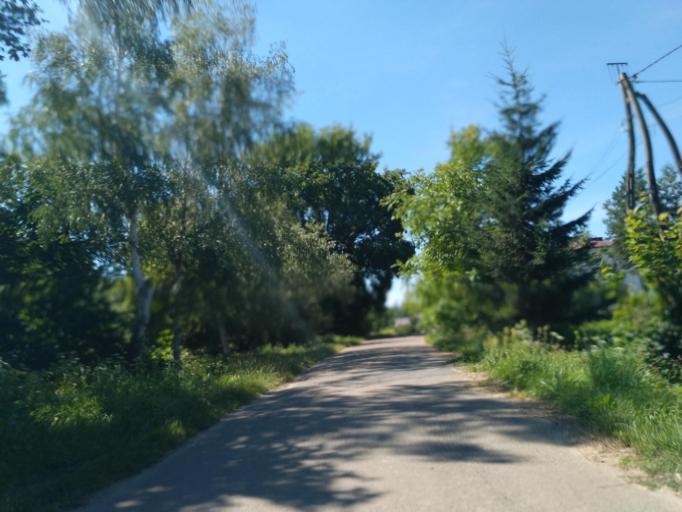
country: PL
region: Subcarpathian Voivodeship
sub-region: Powiat sanocki
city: Nowosielce-Gniewosz
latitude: 49.5303
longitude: 22.0452
